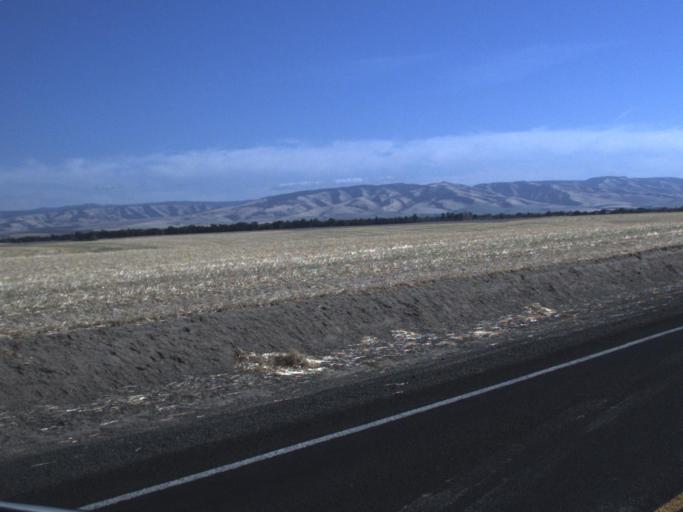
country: US
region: Washington
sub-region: Walla Walla County
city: Walla Walla
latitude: 46.0934
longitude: -118.3677
